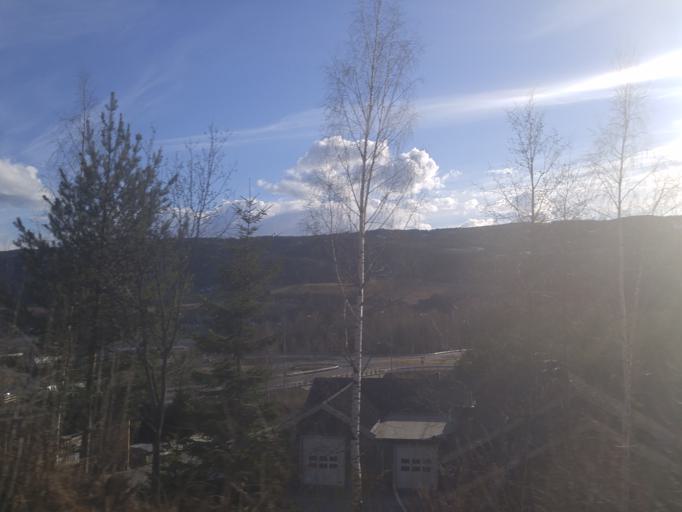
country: NO
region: Oppland
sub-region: Lillehammer
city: Lillehammer
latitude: 61.1323
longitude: 10.4356
